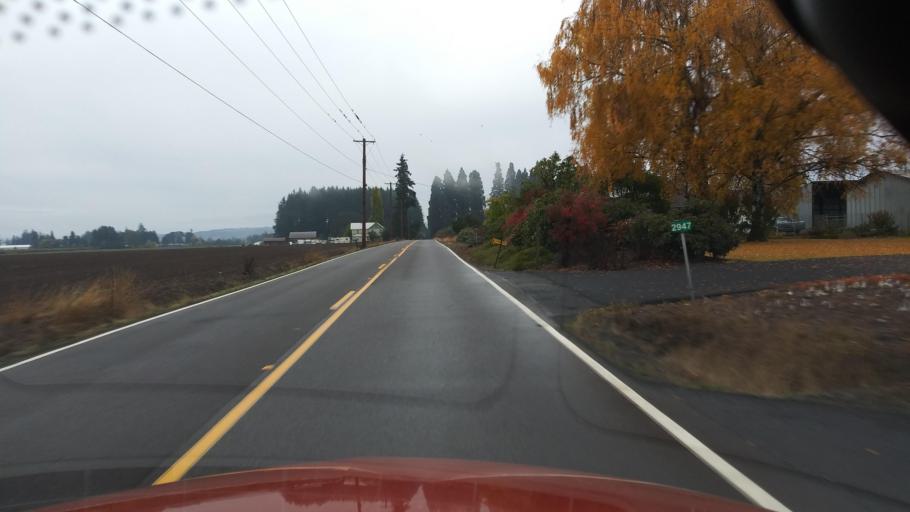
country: US
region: Oregon
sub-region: Washington County
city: Forest Grove
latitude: 45.5421
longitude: -123.0870
